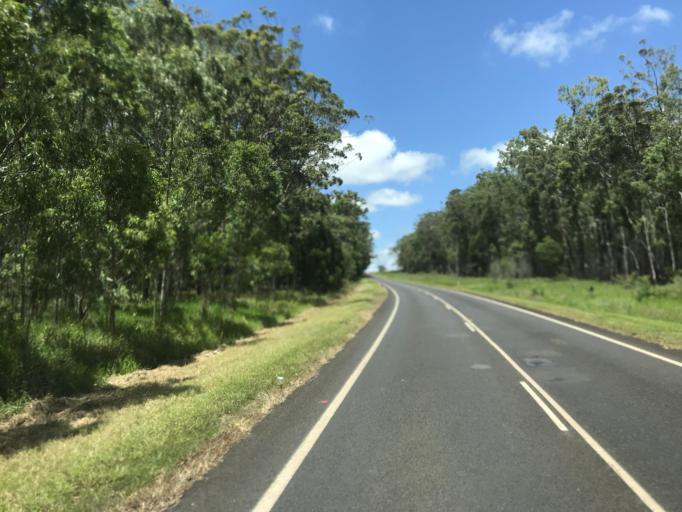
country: AU
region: Queensland
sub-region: Tablelands
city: Ravenshoe
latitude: -17.5360
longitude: 145.4519
